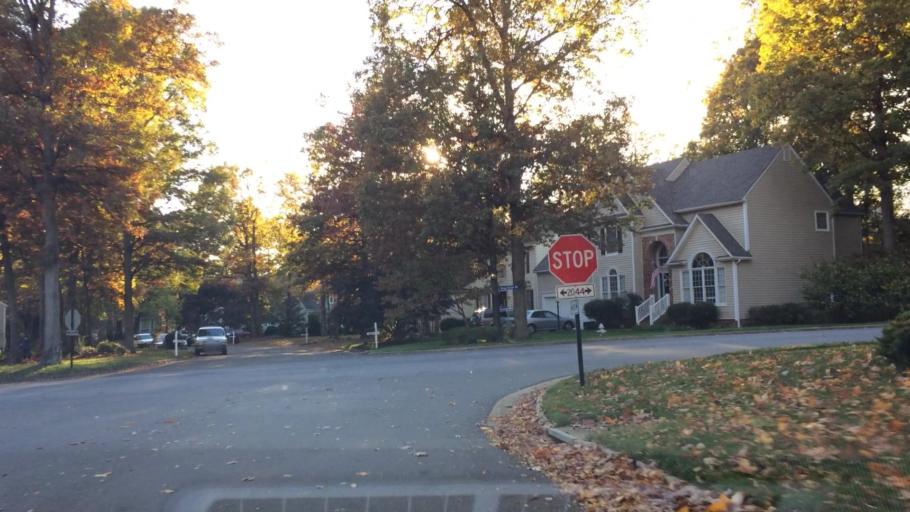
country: US
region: Virginia
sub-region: Henrico County
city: Chamberlayne
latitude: 37.6870
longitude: -77.4187
